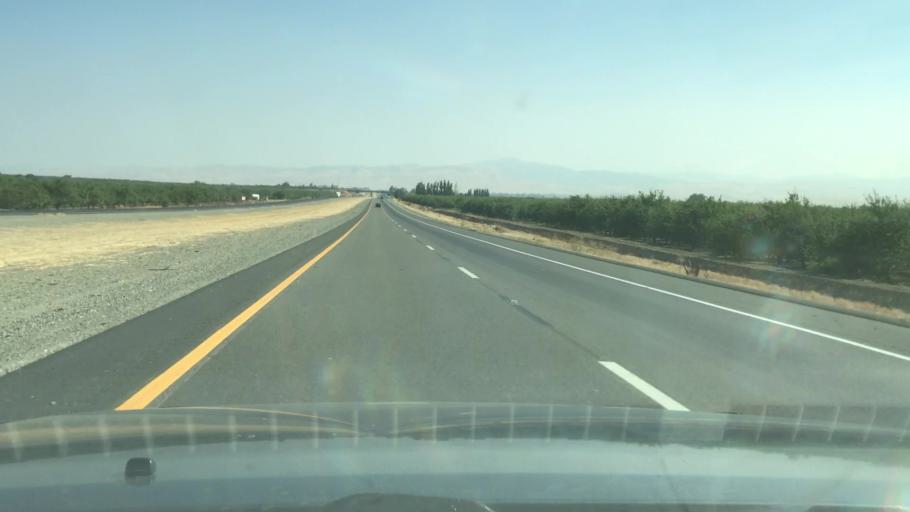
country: US
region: California
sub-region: San Joaquin County
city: Tracy
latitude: 37.6775
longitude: -121.3434
